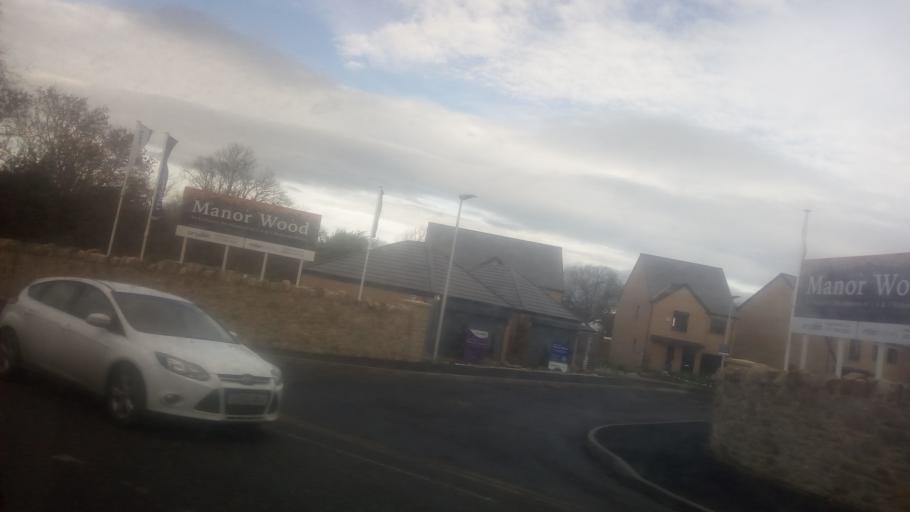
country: GB
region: Scotland
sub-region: Midlothian
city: Bonnyrigg
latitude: 55.9143
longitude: -3.1271
